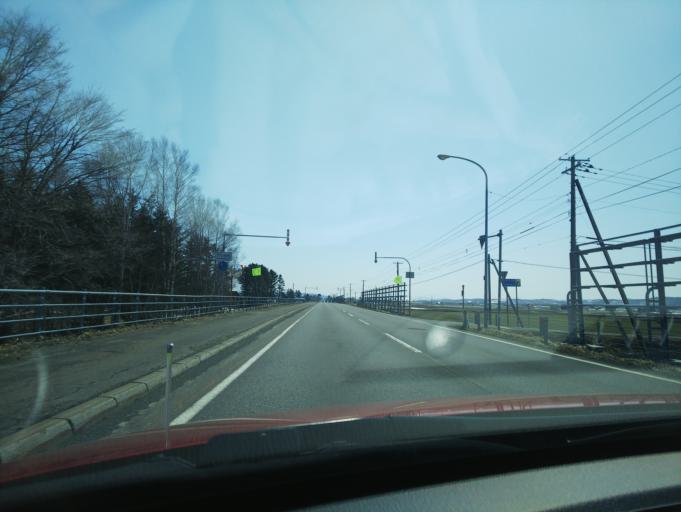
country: JP
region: Hokkaido
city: Nayoro
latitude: 44.2211
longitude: 142.3949
